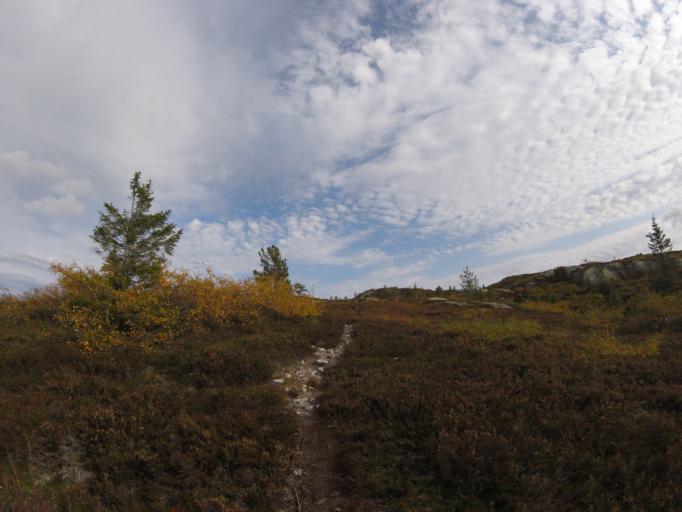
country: NO
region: Buskerud
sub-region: Rollag
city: Rollag
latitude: 59.7984
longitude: 9.3459
